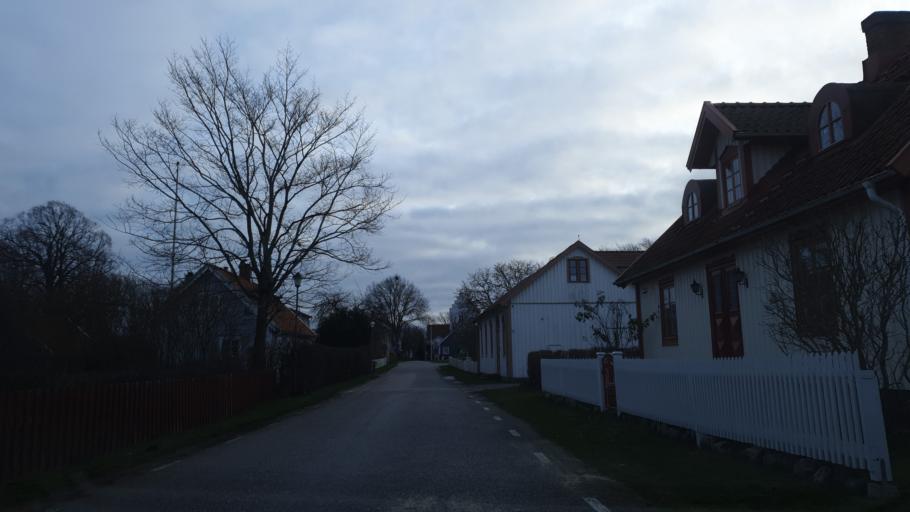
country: SE
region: Kalmar
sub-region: Torsas Kommun
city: Torsas
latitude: 56.2589
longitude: 16.0413
